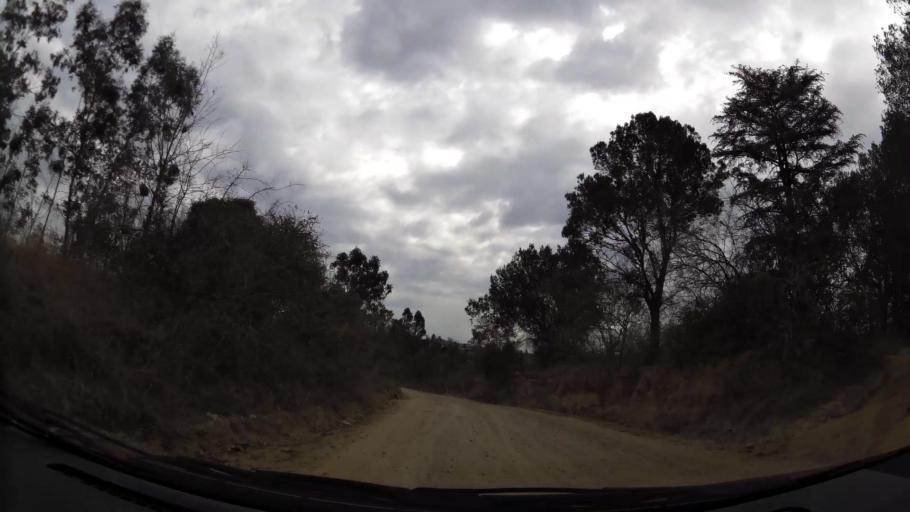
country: ZA
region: Gauteng
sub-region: West Rand District Municipality
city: Muldersdriseloop
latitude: -26.0387
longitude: 27.8516
